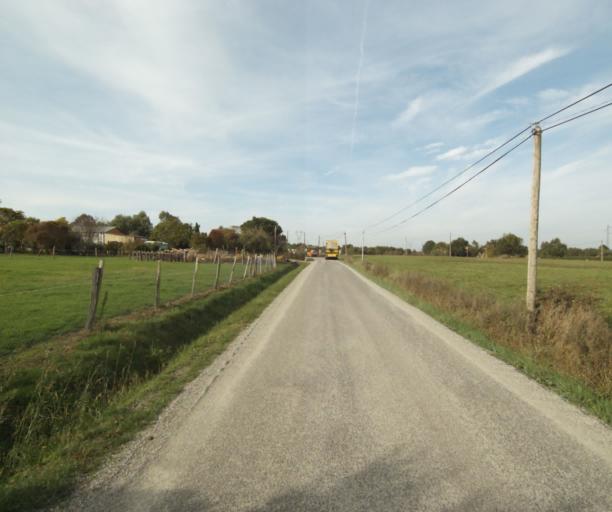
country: FR
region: Midi-Pyrenees
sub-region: Departement du Tarn-et-Garonne
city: Campsas
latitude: 43.9109
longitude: 1.3309
